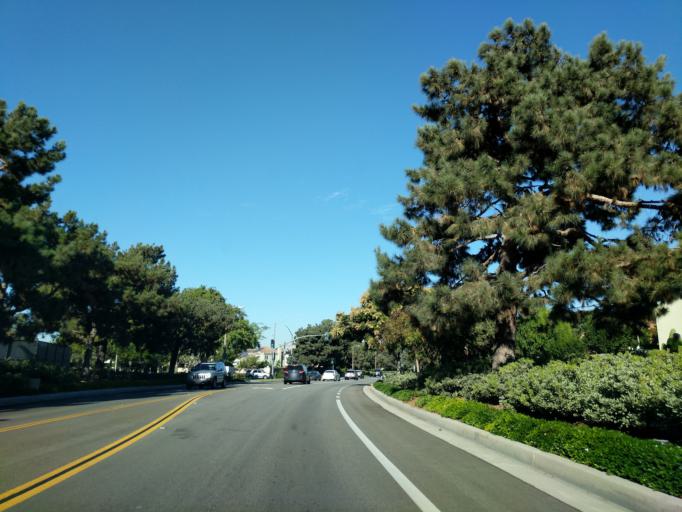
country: US
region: California
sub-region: Orange County
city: Irvine
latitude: 33.6795
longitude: -117.8201
